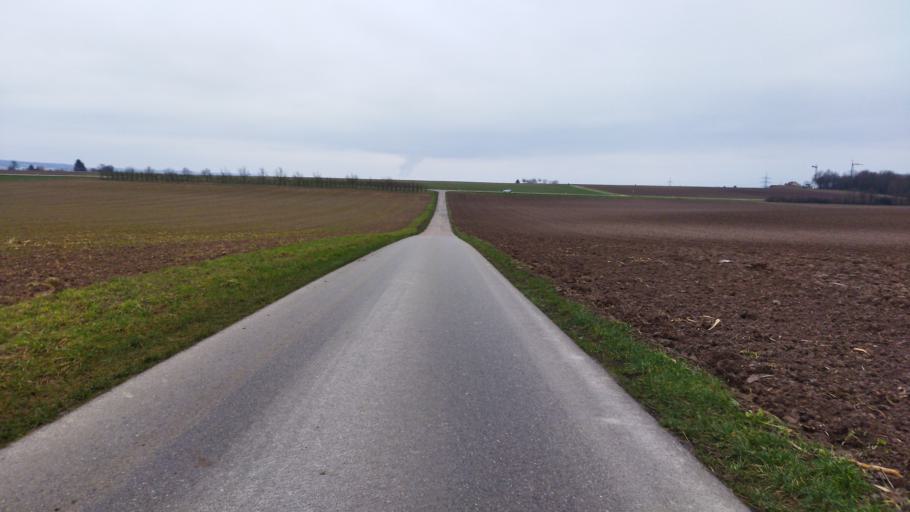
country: DE
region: Baden-Wuerttemberg
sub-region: Regierungsbezirk Stuttgart
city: Nordheim
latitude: 49.1298
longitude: 9.1581
